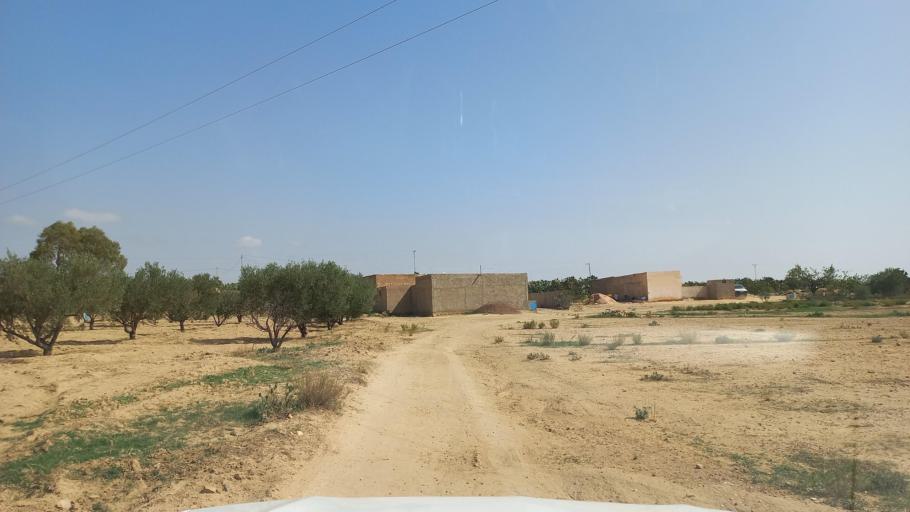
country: TN
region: Al Qasrayn
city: Sbiba
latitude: 35.3926
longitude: 8.9575
